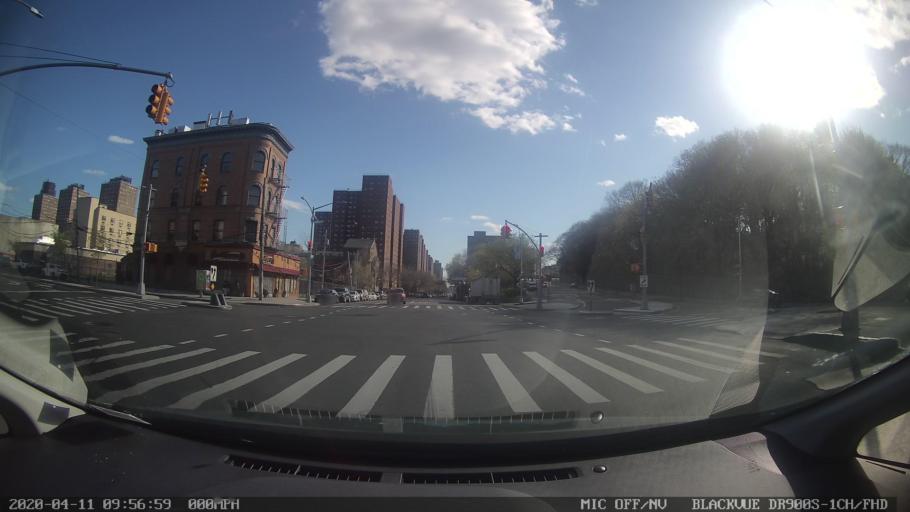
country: US
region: New York
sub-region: New York County
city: Inwood
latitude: 40.8399
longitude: -73.9054
